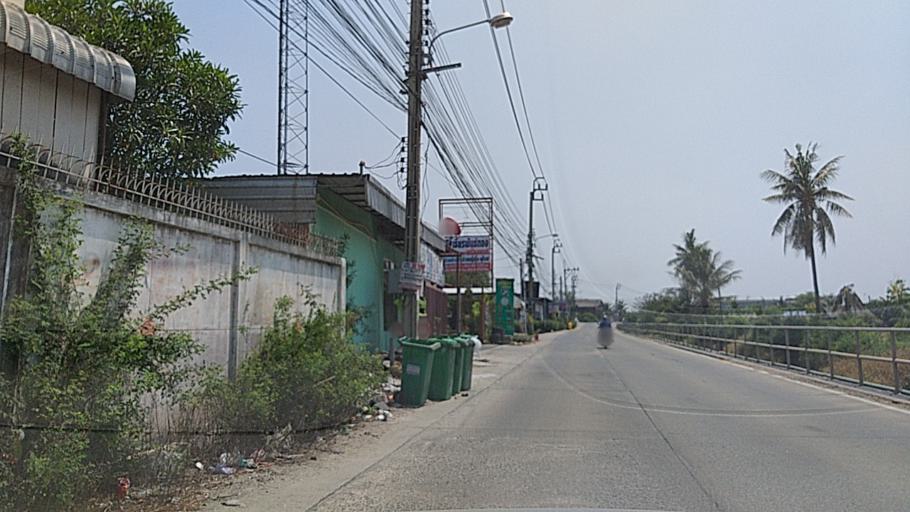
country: TH
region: Nonthaburi
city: Bang Bua Thong
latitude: 13.9149
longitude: 100.3980
